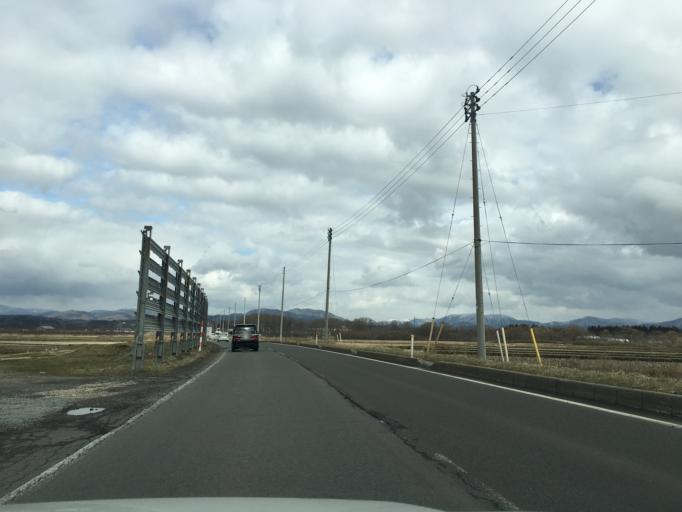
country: JP
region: Akita
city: Hanawa
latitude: 40.2502
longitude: 140.7575
